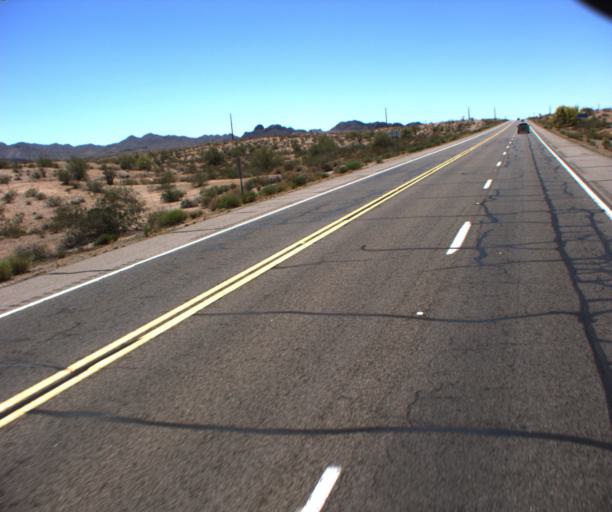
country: US
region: Arizona
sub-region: Mohave County
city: Desert Hills
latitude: 34.6752
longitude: -114.3085
